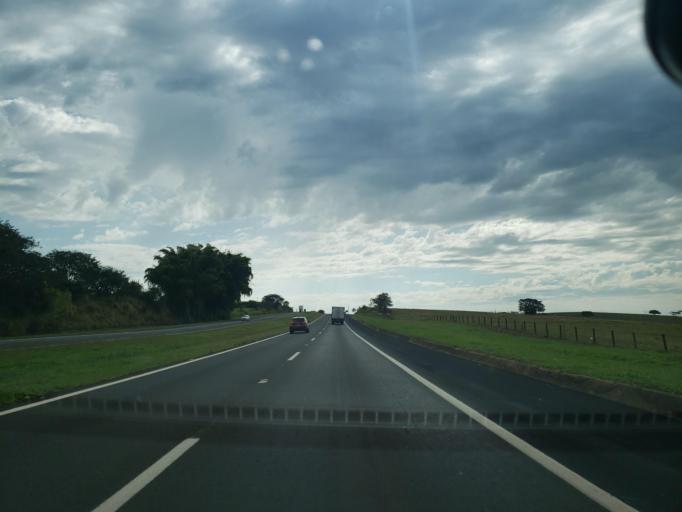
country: BR
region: Sao Paulo
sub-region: Cafelandia
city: Cafelandia
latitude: -21.7831
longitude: -49.6565
